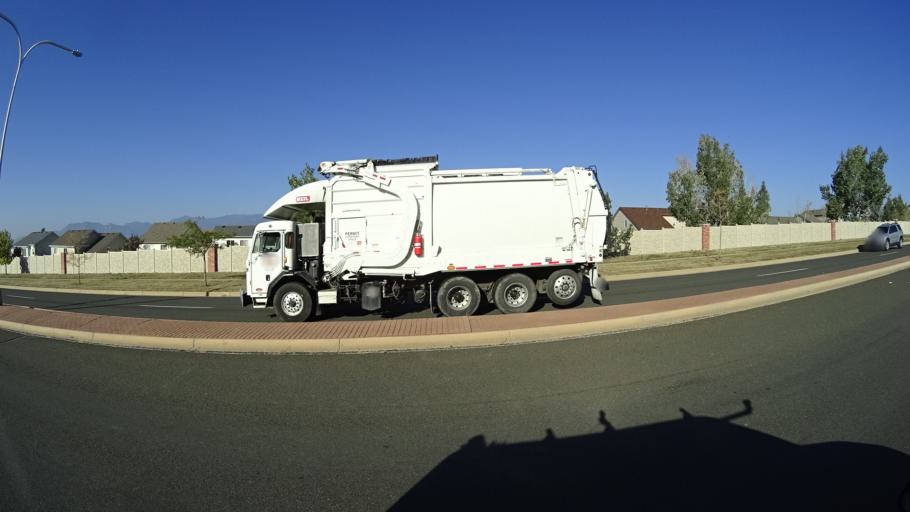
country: US
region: Colorado
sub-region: El Paso County
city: Cimarron Hills
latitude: 38.8916
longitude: -104.7018
